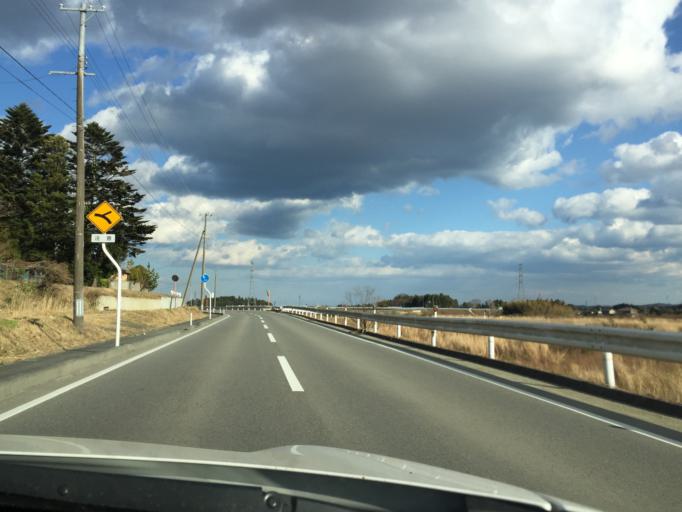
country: JP
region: Fukushima
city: Namie
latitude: 37.4132
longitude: 140.9568
